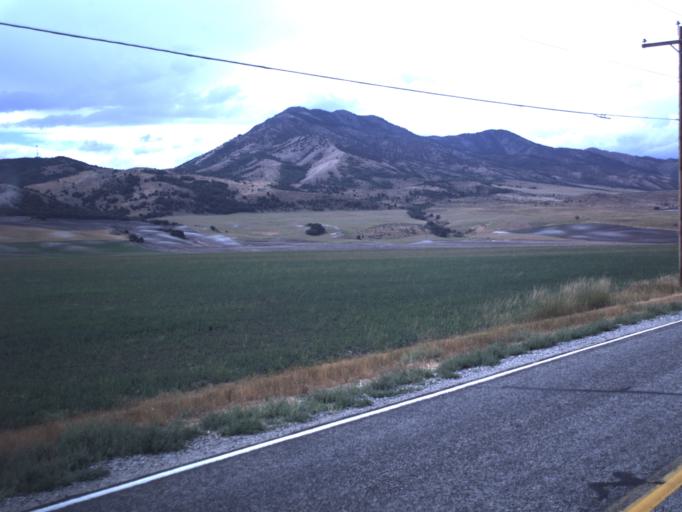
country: US
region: Utah
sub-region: Cache County
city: Benson
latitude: 41.8932
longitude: -112.0415
